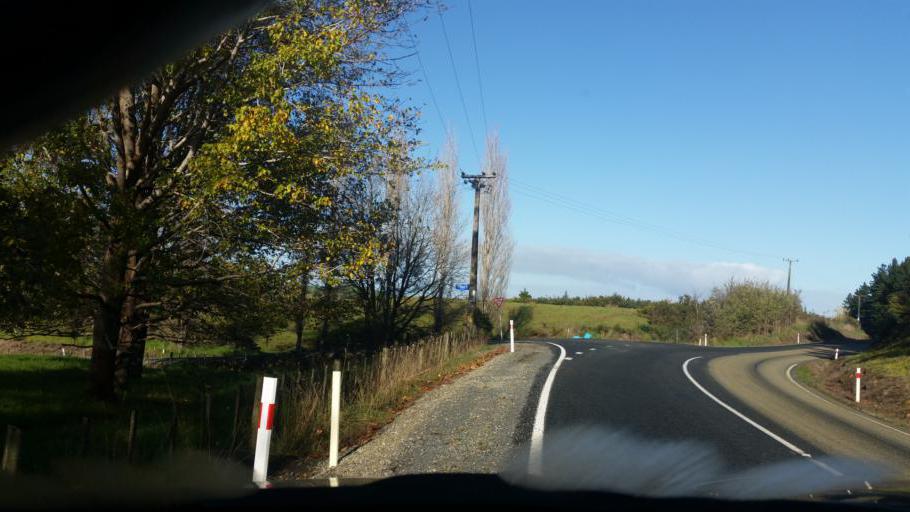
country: NZ
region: Auckland
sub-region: Auckland
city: Wellsford
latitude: -36.2297
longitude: 174.4460
